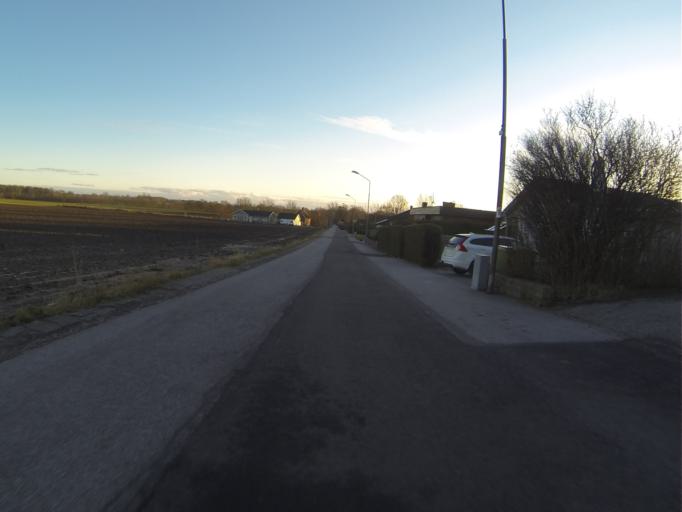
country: SE
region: Skane
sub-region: Lunds Kommun
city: Lund
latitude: 55.7904
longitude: 13.2077
